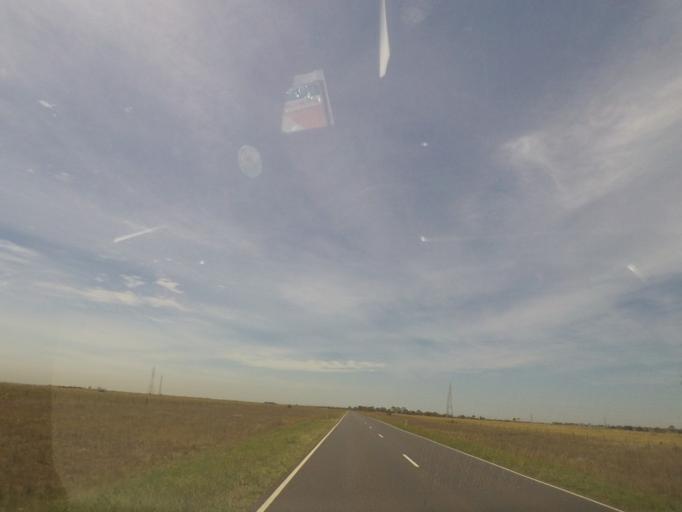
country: AU
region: Victoria
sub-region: Wyndham
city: Wyndham Vale
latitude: -37.8271
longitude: 144.5374
